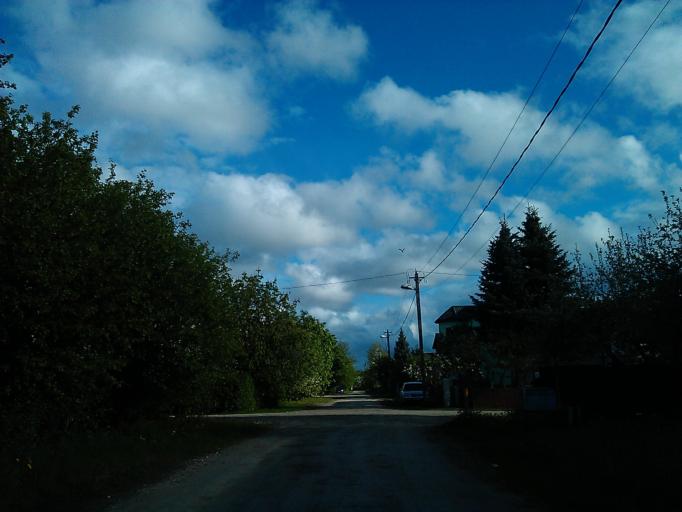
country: LV
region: Adazi
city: Adazi
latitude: 57.0720
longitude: 24.3259
